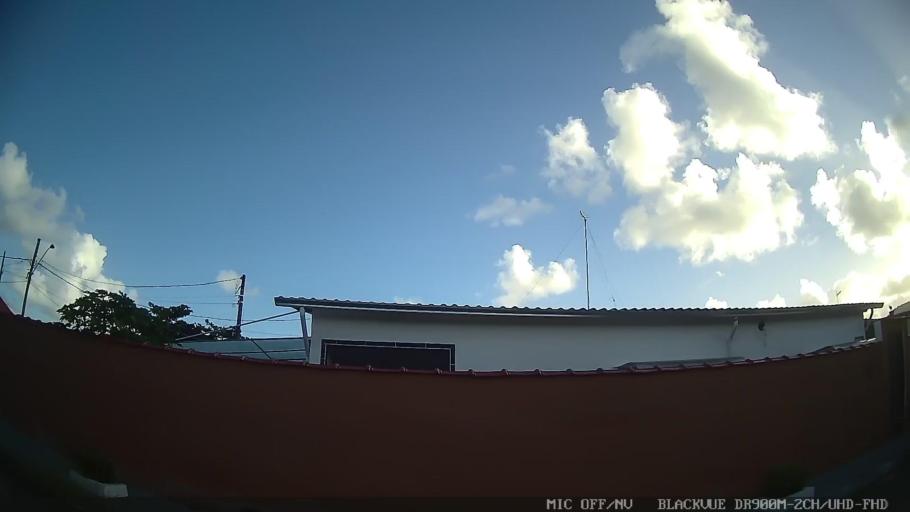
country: BR
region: Sao Paulo
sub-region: Itanhaem
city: Itanhaem
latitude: -24.1371
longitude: -46.7184
